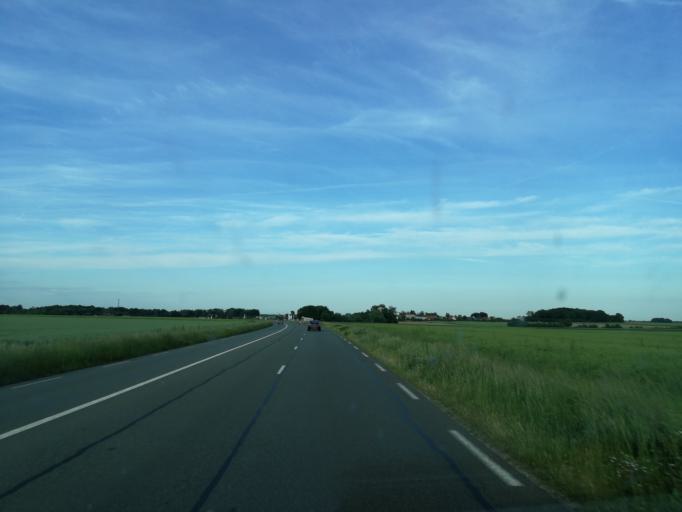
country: FR
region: Centre
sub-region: Departement d'Eure-et-Loir
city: Auneau
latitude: 48.5041
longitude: 1.7498
